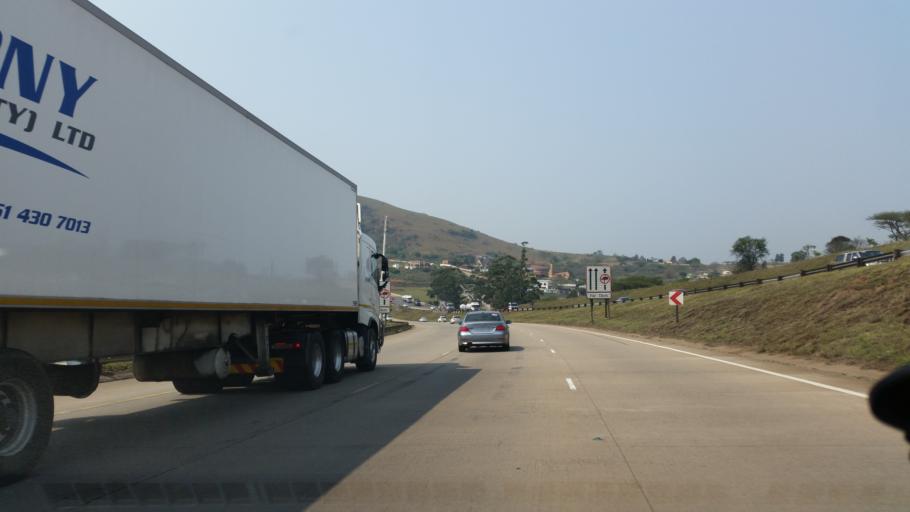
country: ZA
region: KwaZulu-Natal
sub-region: eThekwini Metropolitan Municipality
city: Mpumalanga
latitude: -29.7678
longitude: 30.6819
